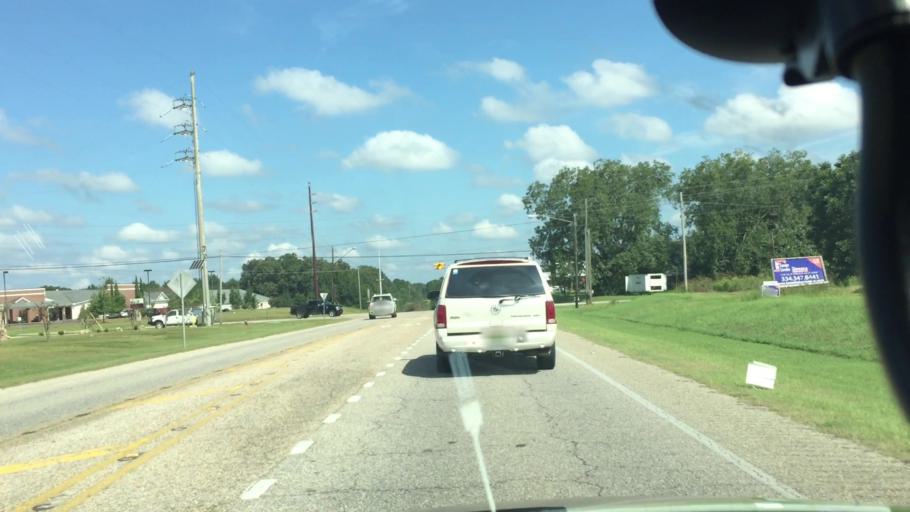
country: US
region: Alabama
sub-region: Coffee County
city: Enterprise
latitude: 31.3597
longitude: -85.8668
